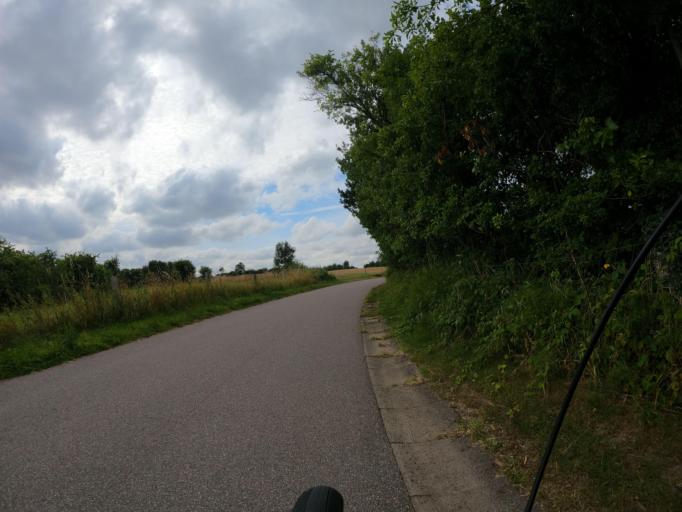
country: DE
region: Schleswig-Holstein
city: Niesgrau
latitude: 54.7439
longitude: 9.7983
